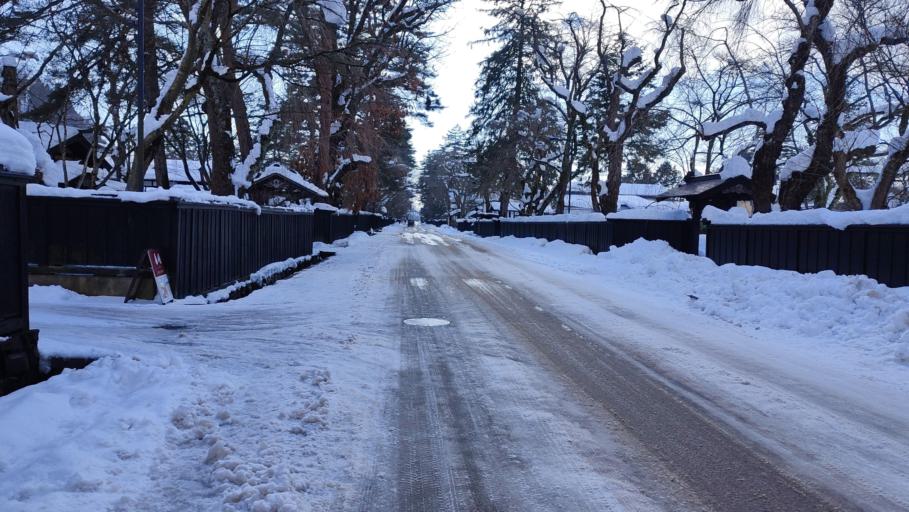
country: JP
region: Akita
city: Kakunodatemachi
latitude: 39.5989
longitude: 140.5619
